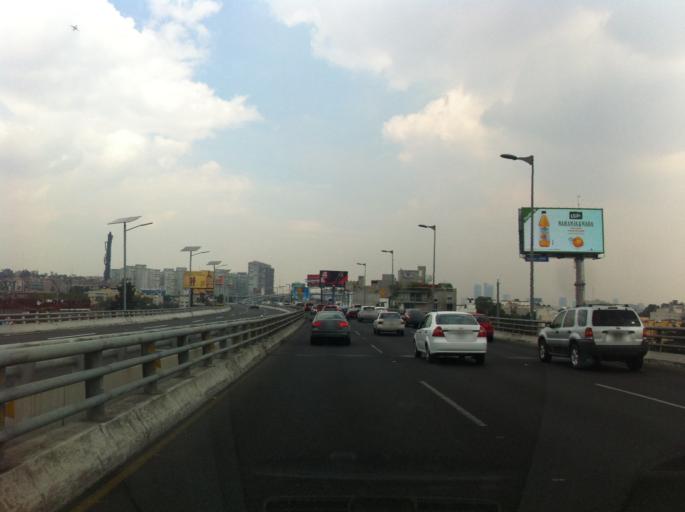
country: MX
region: Mexico City
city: Alvaro Obregon
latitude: 19.3766
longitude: -99.1917
